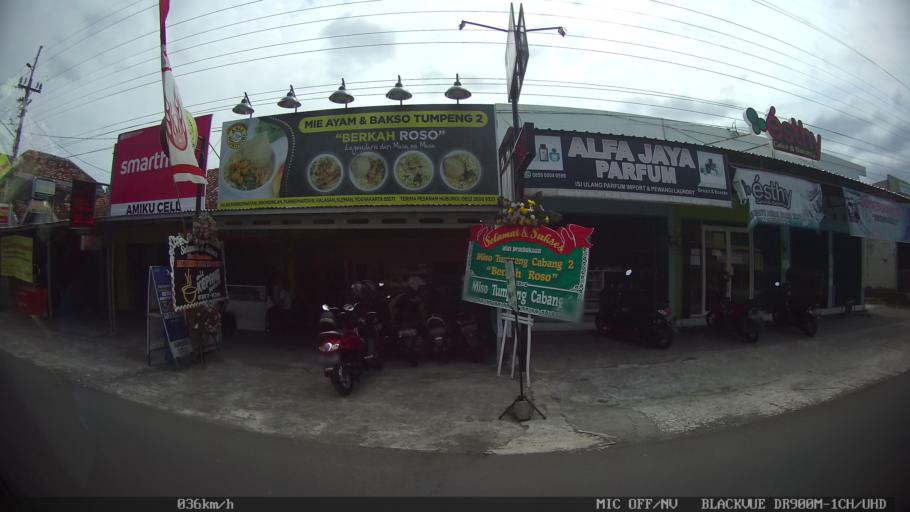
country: ID
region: Daerah Istimewa Yogyakarta
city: Depok
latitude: -7.7477
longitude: 110.4492
